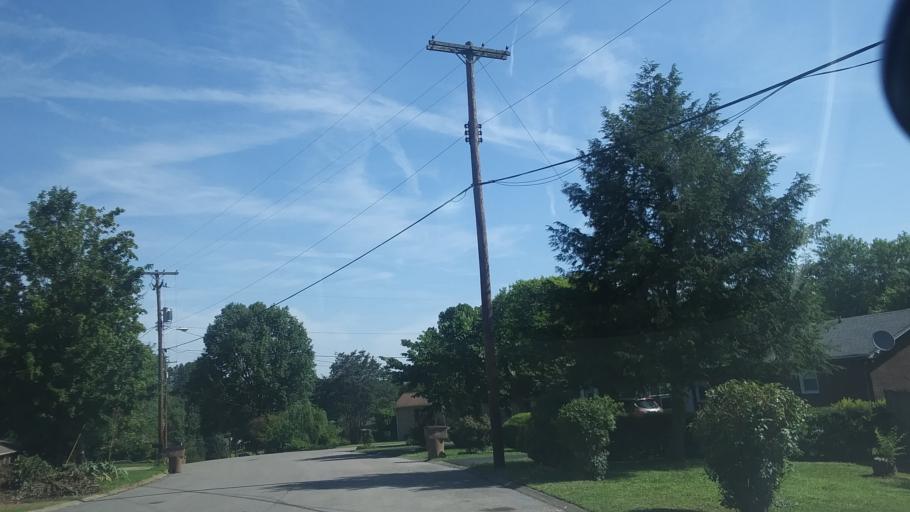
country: US
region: Tennessee
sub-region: Davidson County
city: Oak Hill
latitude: 36.0792
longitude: -86.7075
